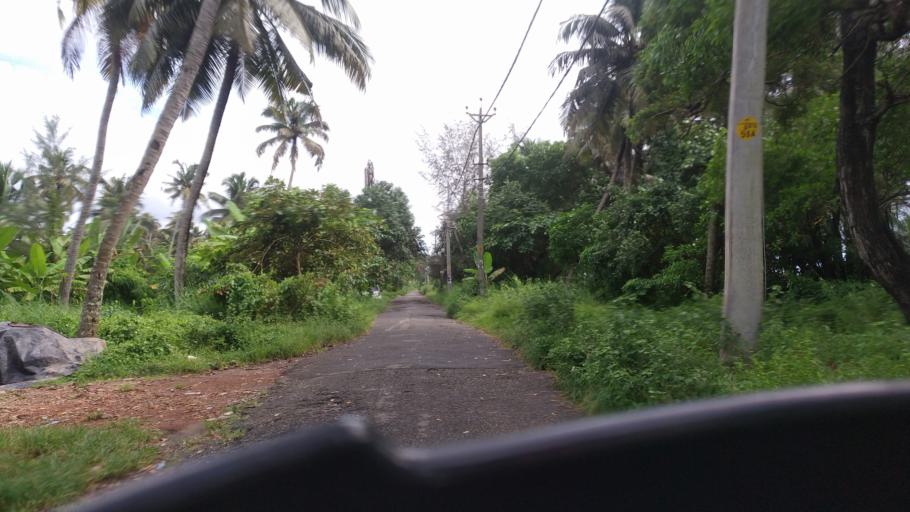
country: IN
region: Kerala
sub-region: Thrissur District
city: Kodungallur
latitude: 10.1169
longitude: 76.1860
